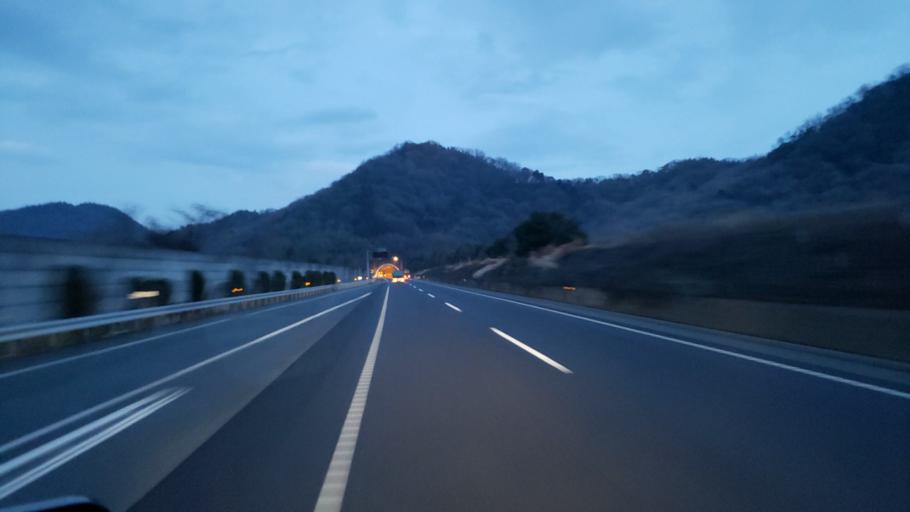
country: JP
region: Hyogo
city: Himeji
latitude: 34.8526
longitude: 134.7666
